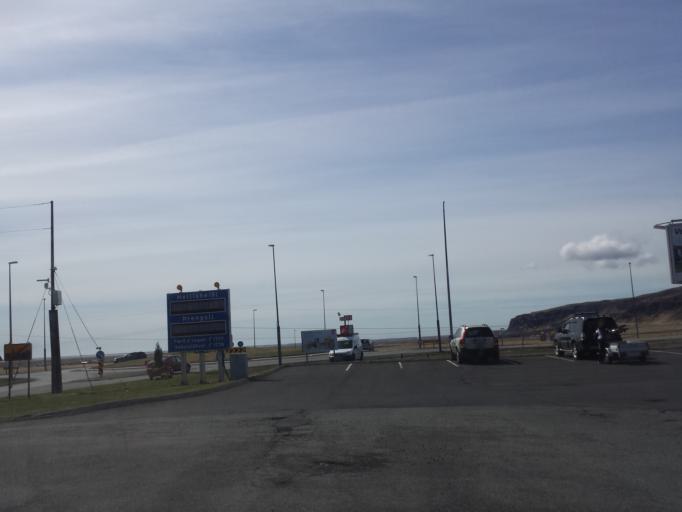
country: IS
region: South
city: Hveragerdi
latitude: 63.9959
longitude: -21.1924
